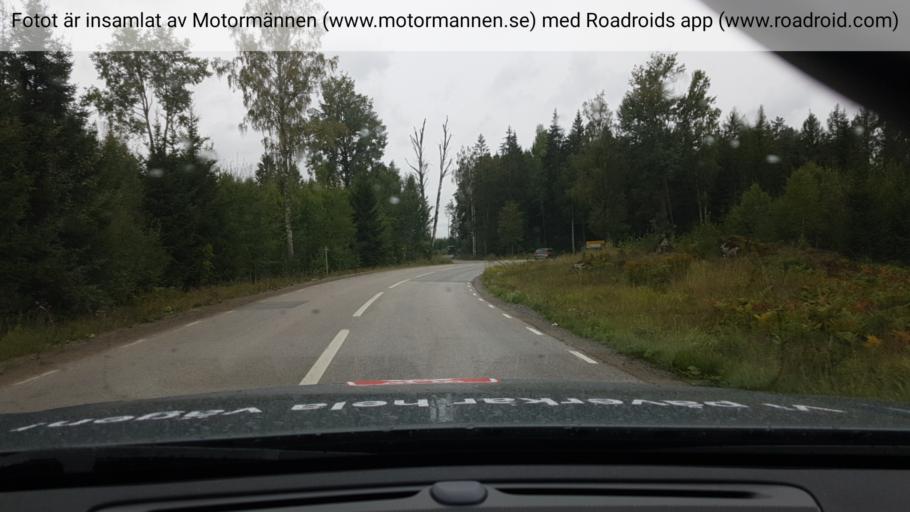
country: SE
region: Stockholm
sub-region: Botkyrka Kommun
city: Tullinge
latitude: 59.1268
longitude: 17.9095
